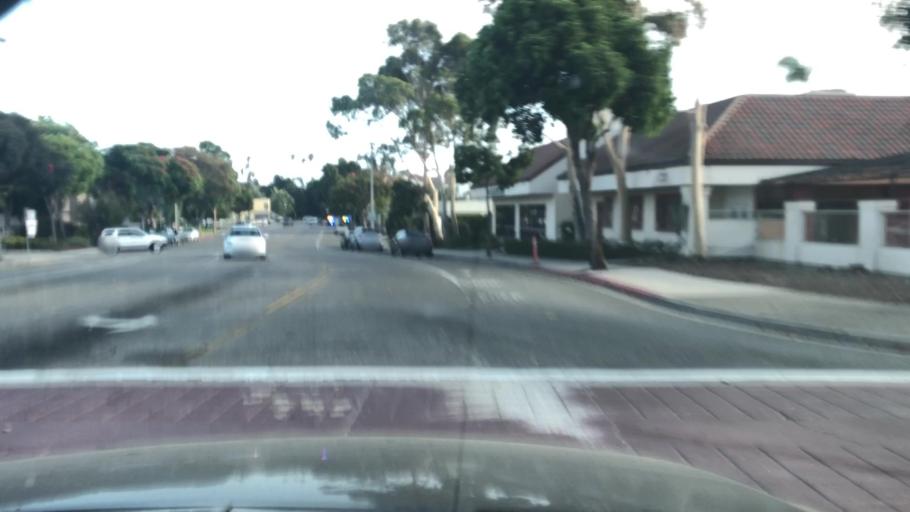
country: US
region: California
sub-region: Ventura County
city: Ventura
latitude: 34.2812
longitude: -119.3024
